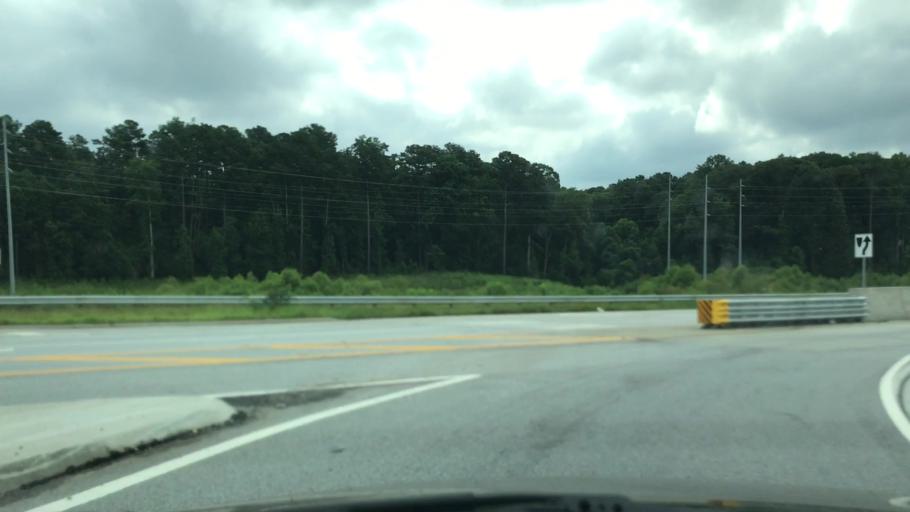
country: US
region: Georgia
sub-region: Gwinnett County
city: Lawrenceville
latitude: 33.9804
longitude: -83.9951
